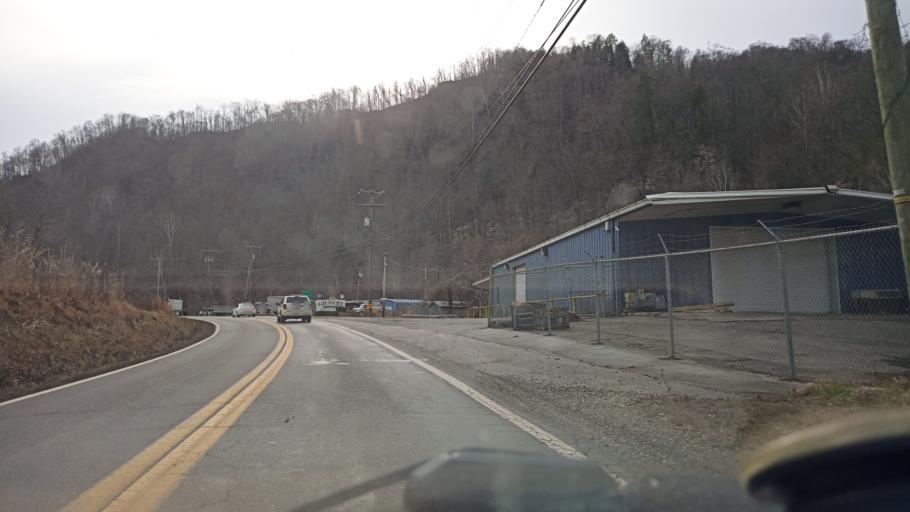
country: US
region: West Virginia
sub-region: Mingo County
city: Gilbert Creek
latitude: 37.6244
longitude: -81.8689
